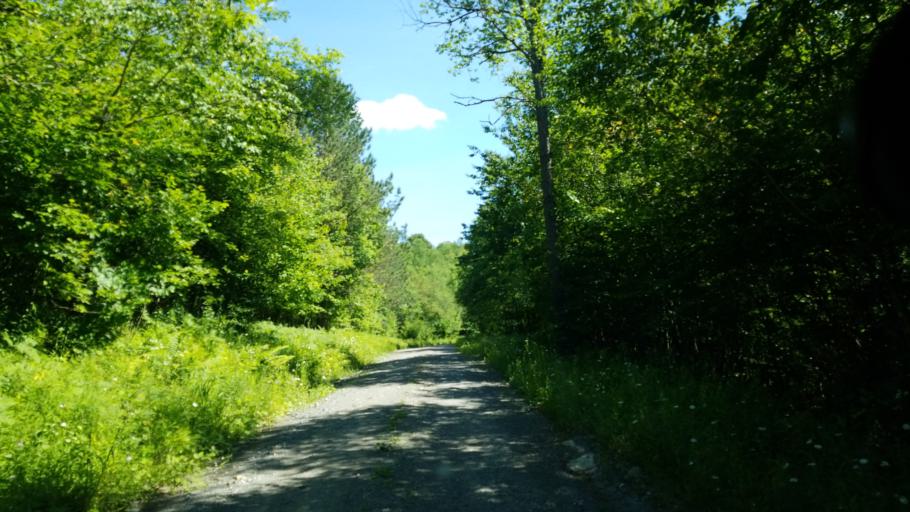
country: US
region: Pennsylvania
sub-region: Clearfield County
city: Clearfield
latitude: 41.2136
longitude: -78.3861
